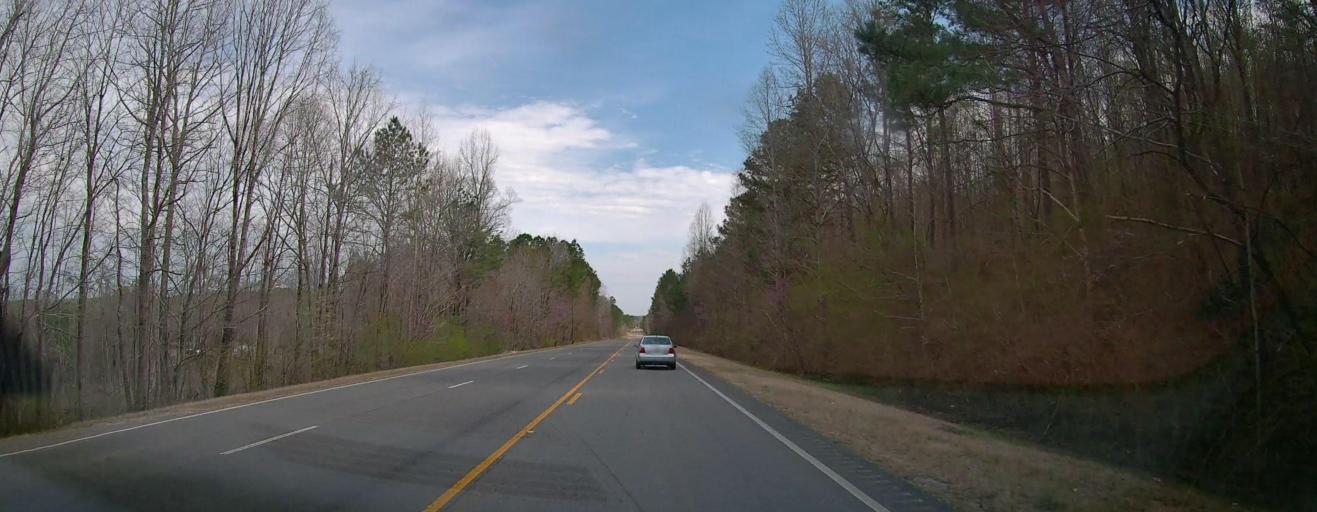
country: US
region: Alabama
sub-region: Walker County
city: Carbon Hill
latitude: 33.9138
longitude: -87.5634
